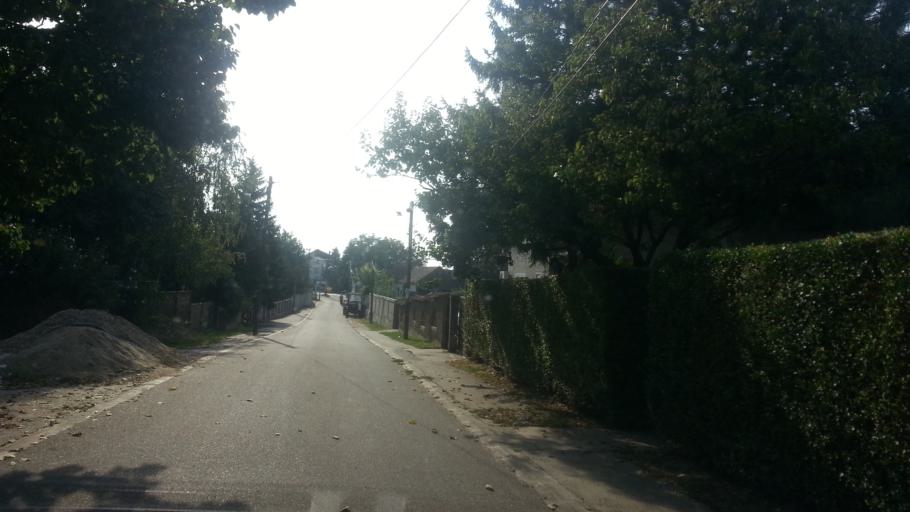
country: RS
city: Novi Banovci
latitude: 44.9510
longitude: 20.2849
